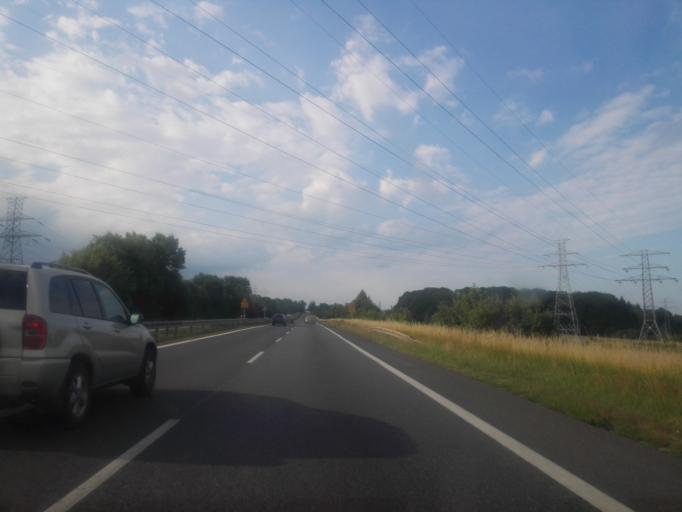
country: PL
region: Silesian Voivodeship
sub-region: Powiat bedzinski
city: Bedzin
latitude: 50.3422
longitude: 19.1103
